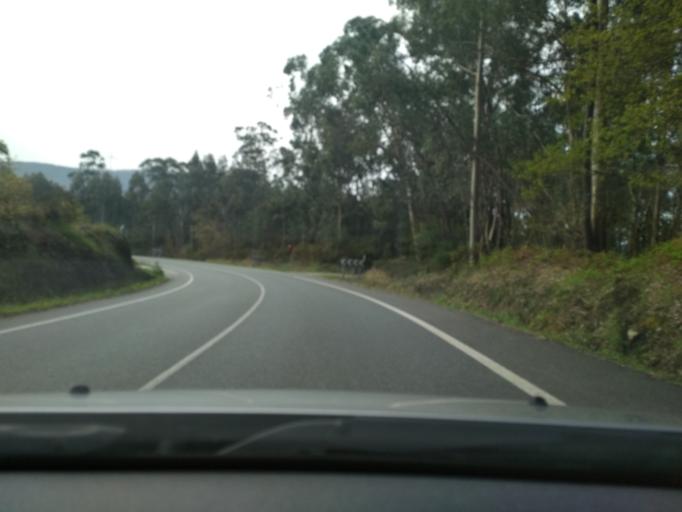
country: ES
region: Galicia
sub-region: Provincia de Pontevedra
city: Catoira
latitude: 42.6638
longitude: -8.7040
